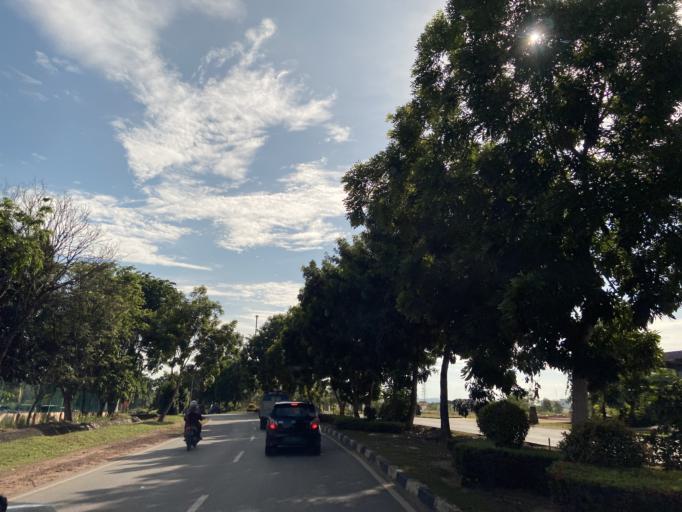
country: SG
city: Singapore
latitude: 1.1216
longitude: 104.0512
